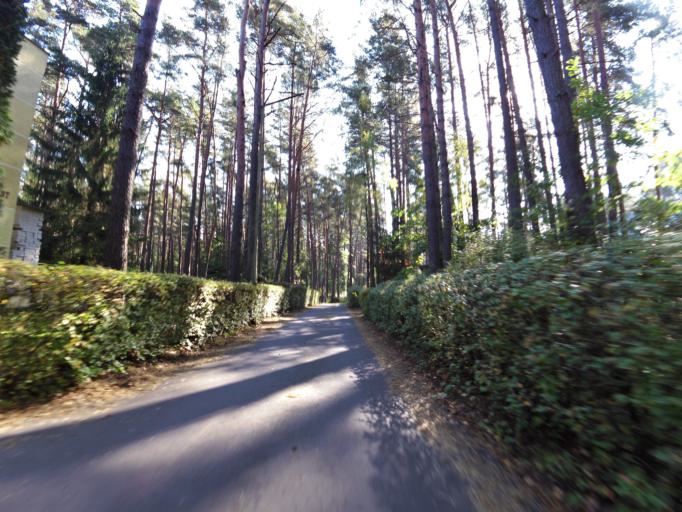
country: LT
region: Vilnius County
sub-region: Vilnius
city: Vilnius
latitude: 54.7344
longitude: 25.3033
